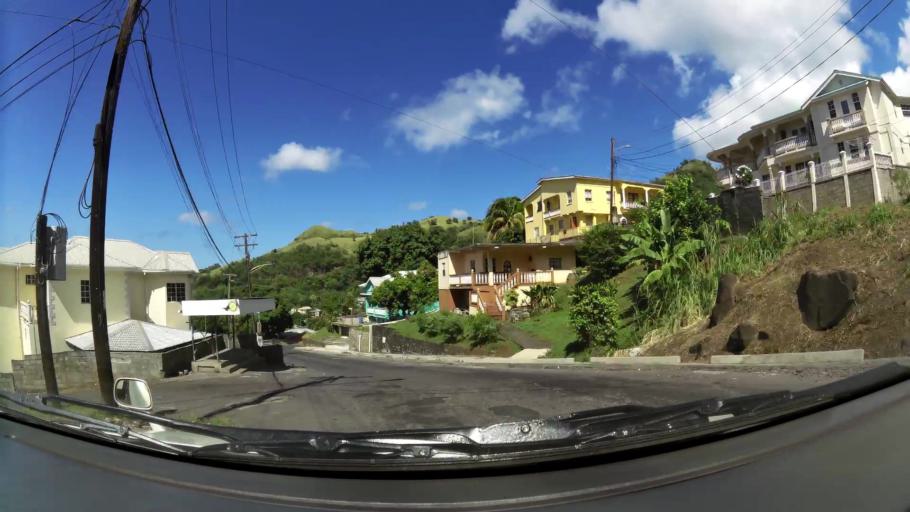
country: VC
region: Saint George
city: Kingstown Park
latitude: 13.1732
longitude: -61.2353
